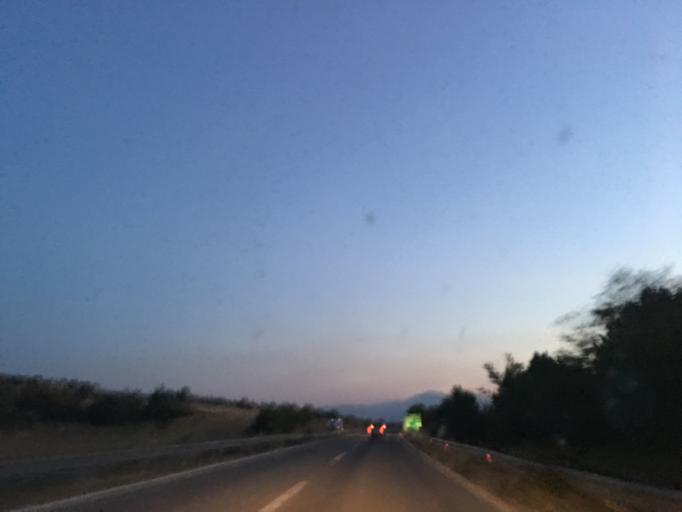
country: MK
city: Miladinovci
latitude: 41.9798
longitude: 21.6524
